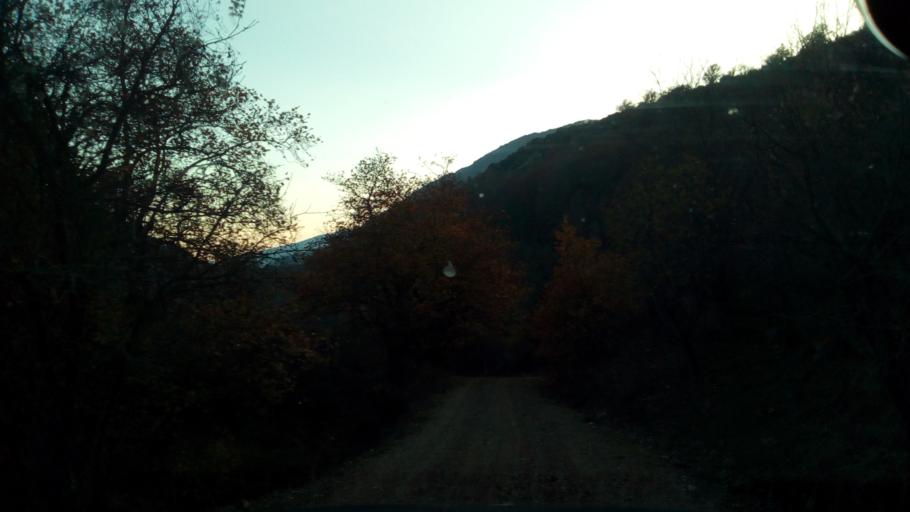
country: GR
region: West Greece
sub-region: Nomos Aitolias kai Akarnanias
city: Nafpaktos
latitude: 38.4708
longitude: 21.8137
